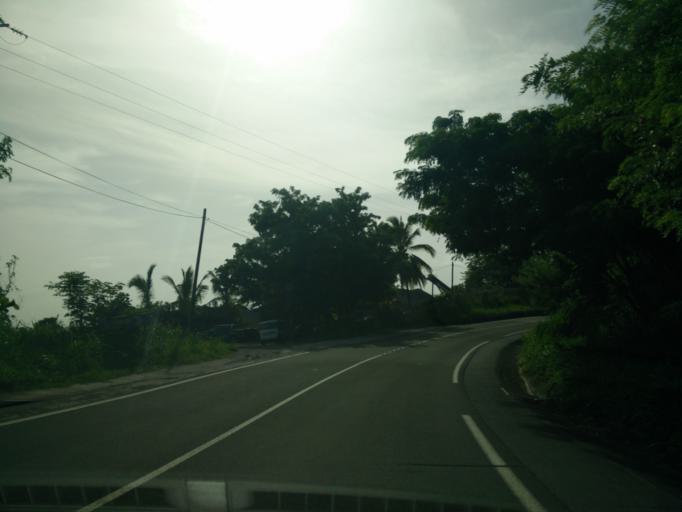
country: MQ
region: Martinique
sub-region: Martinique
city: Saint-Pierre
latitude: 14.7643
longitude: -61.1934
